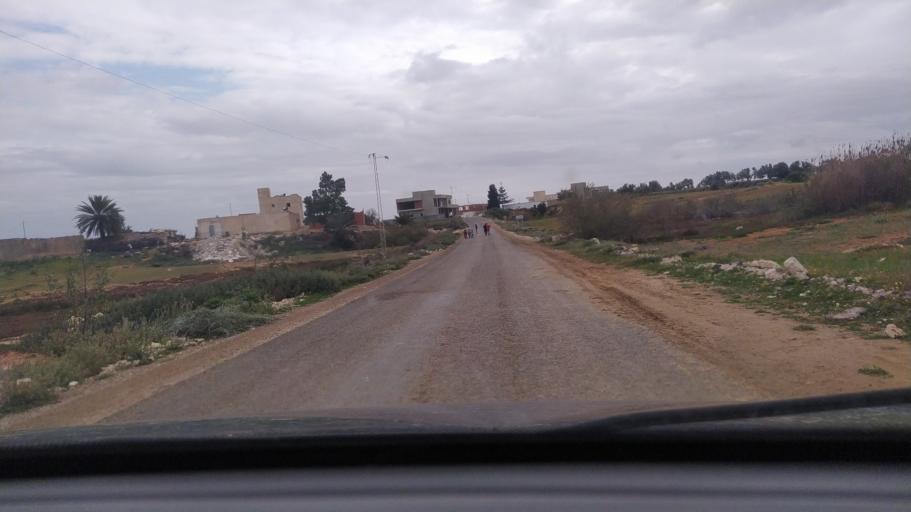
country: TN
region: Al Munastir
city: Sidi Bin Nur
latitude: 35.5167
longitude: 10.9662
